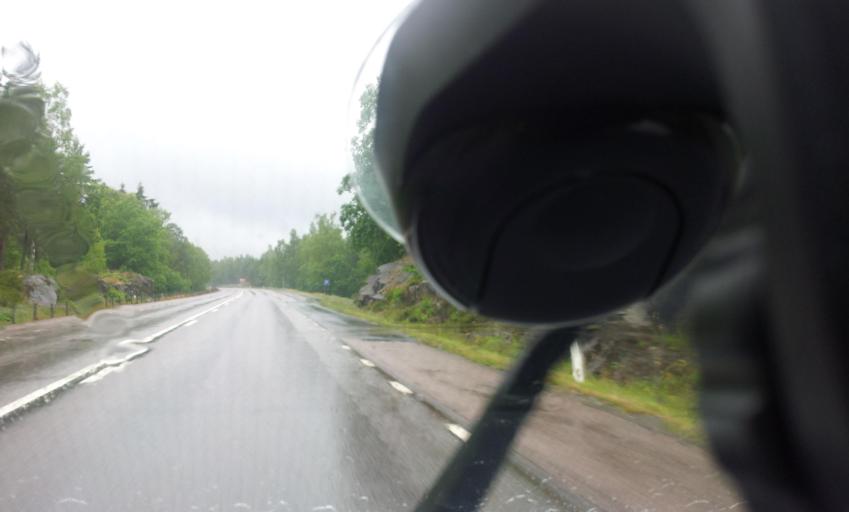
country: SE
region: Kalmar
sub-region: Oskarshamns Kommun
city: Oskarshamn
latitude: 57.5075
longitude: 16.5022
